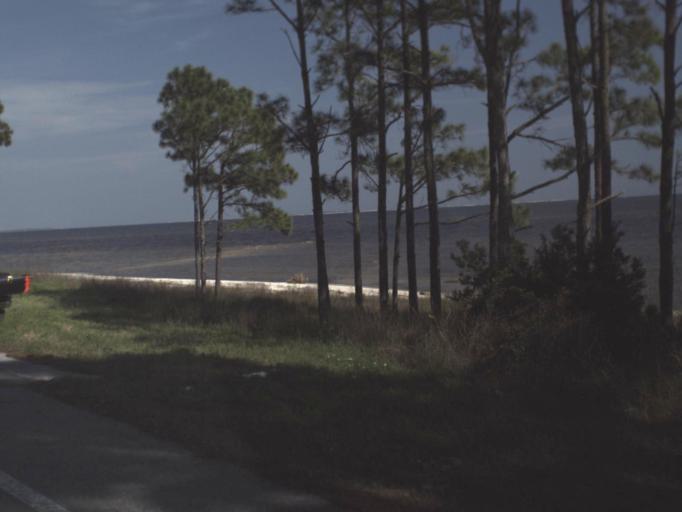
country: US
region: Florida
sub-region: Franklin County
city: Eastpoint
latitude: 29.7809
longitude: -84.7780
